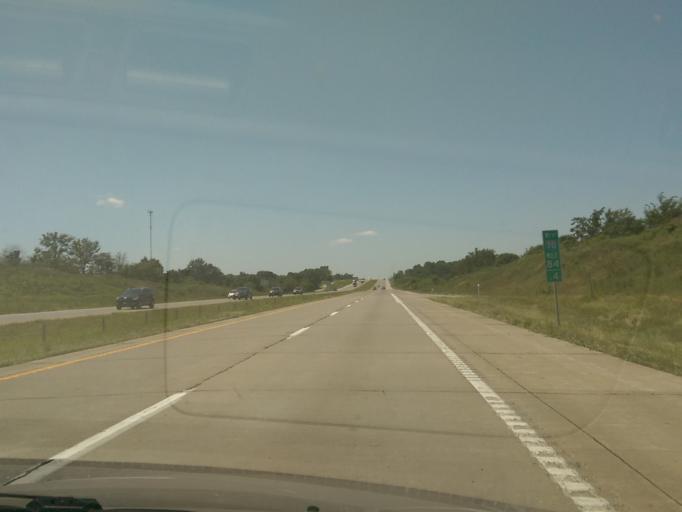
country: US
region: Missouri
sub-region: Saline County
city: Marshall
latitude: 38.9533
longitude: -93.0893
